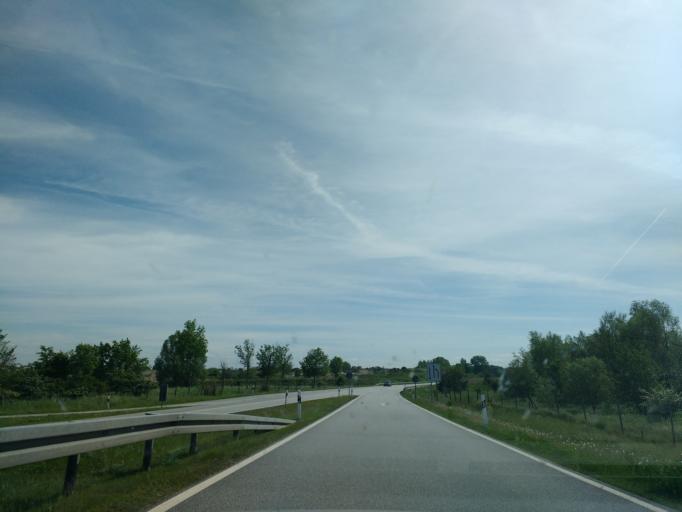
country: DE
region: Mecklenburg-Vorpommern
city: Zurow
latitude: 53.8700
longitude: 11.6211
